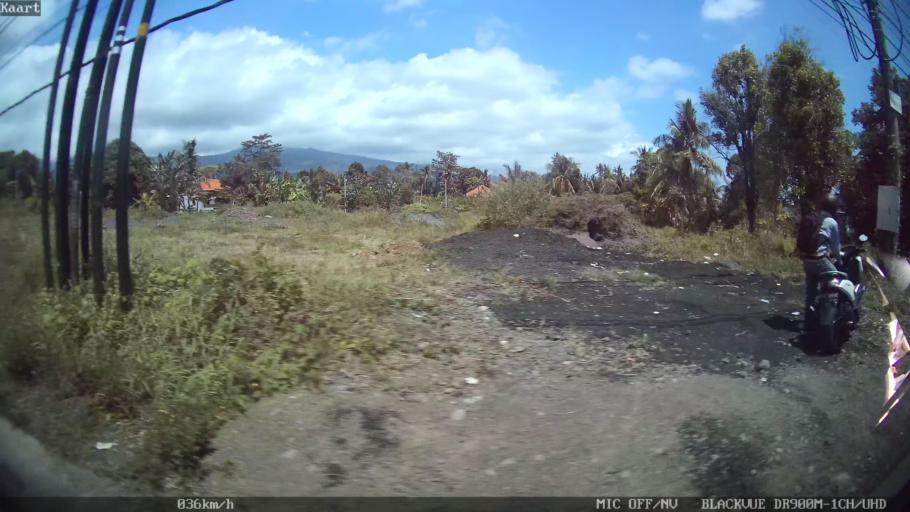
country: ID
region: Bali
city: Banjar Padangbulia
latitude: -8.1571
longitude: 115.1131
